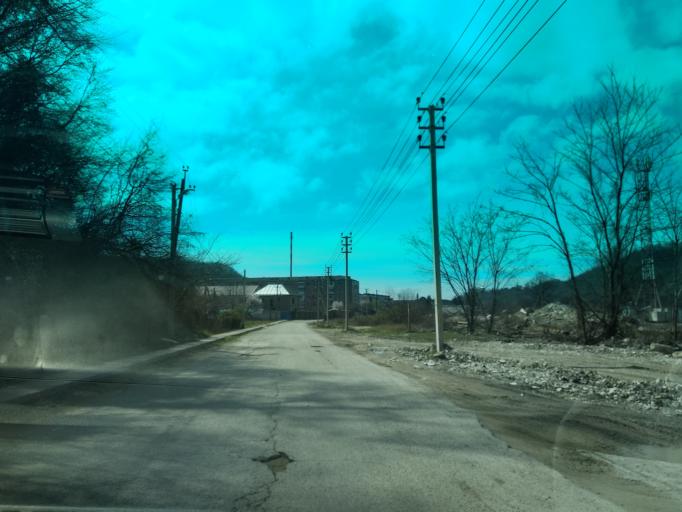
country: RU
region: Krasnodarskiy
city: Shepsi
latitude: 44.0458
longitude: 39.1566
